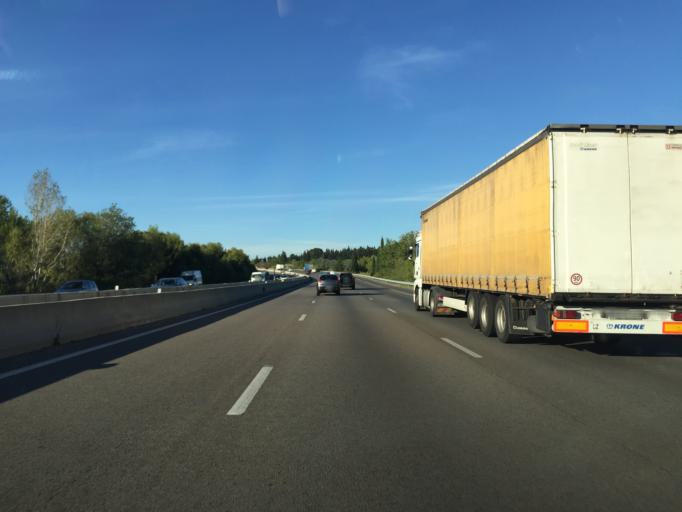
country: FR
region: Provence-Alpes-Cote d'Azur
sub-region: Departement du Vaucluse
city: Morieres-les-Avignon
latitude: 43.9120
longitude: 4.9141
